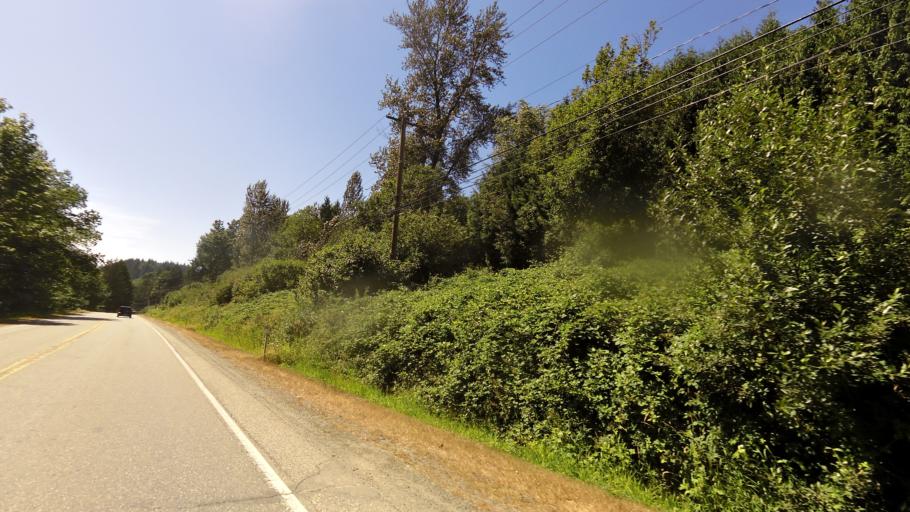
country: CA
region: British Columbia
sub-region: Fraser Valley Regional District
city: Chilliwack
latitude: 49.1944
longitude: -122.0638
